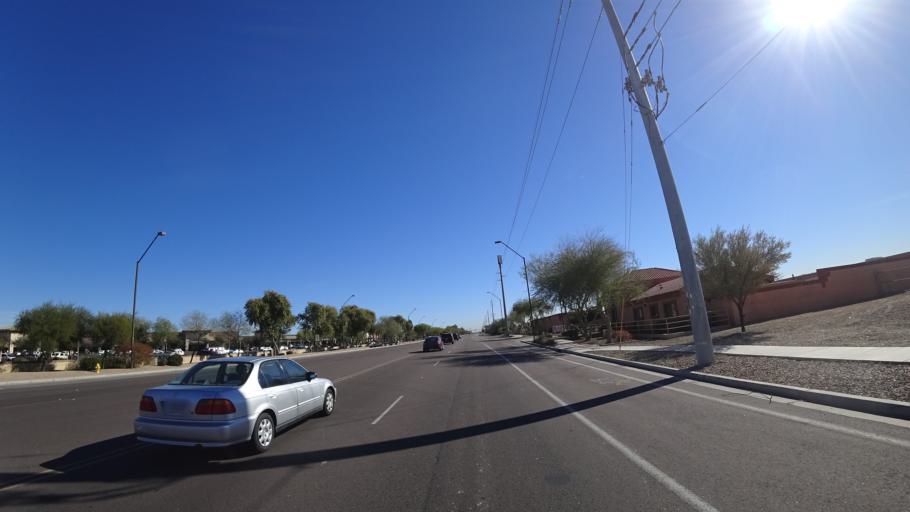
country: US
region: Arizona
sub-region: Maricopa County
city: Litchfield Park
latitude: 33.4932
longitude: -112.3399
